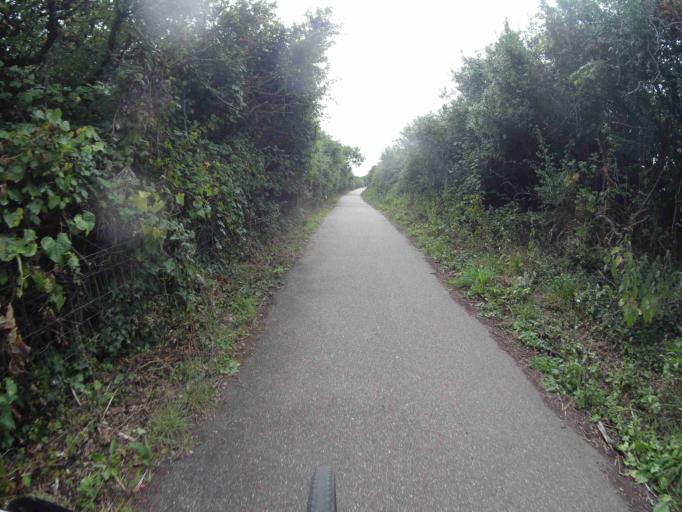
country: GB
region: England
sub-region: Devon
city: Dawlish
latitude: 50.5925
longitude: -3.4455
